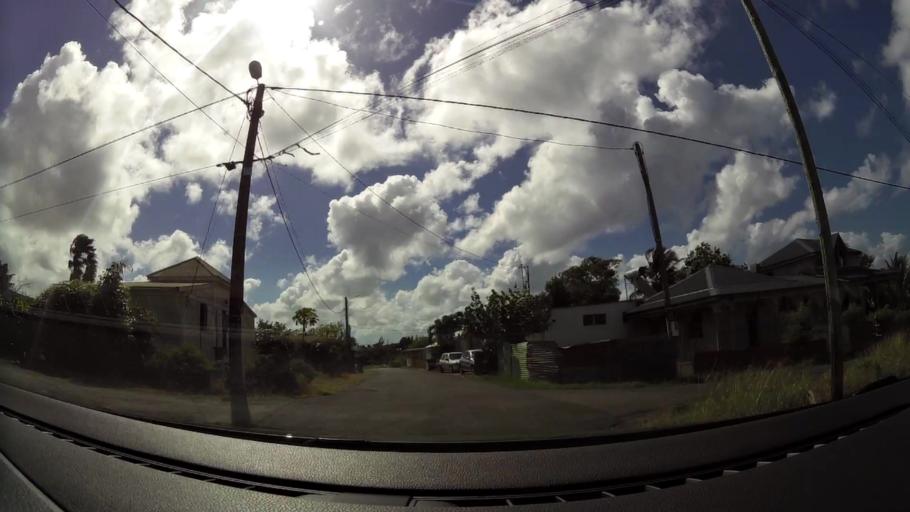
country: GP
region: Guadeloupe
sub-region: Guadeloupe
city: Port-Louis
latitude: 16.4233
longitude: -61.5249
